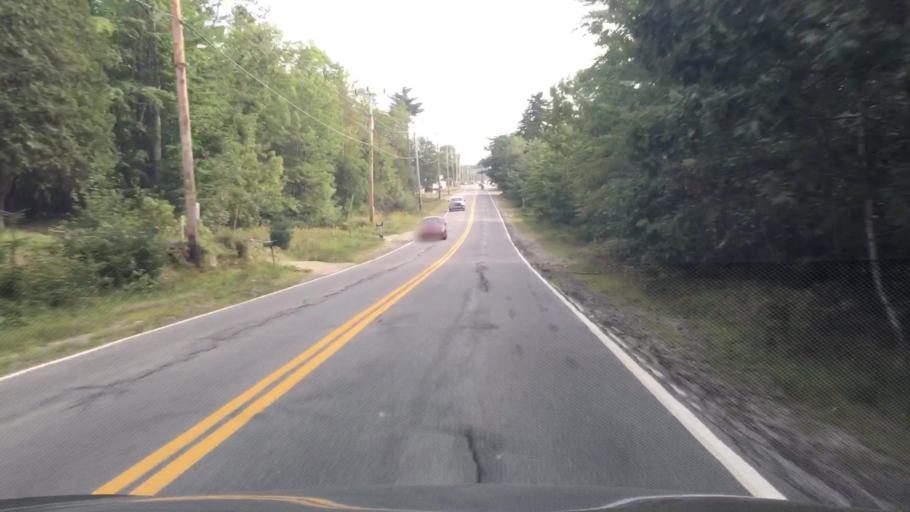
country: US
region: Maine
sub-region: Hancock County
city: Surry
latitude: 44.4339
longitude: -68.5734
